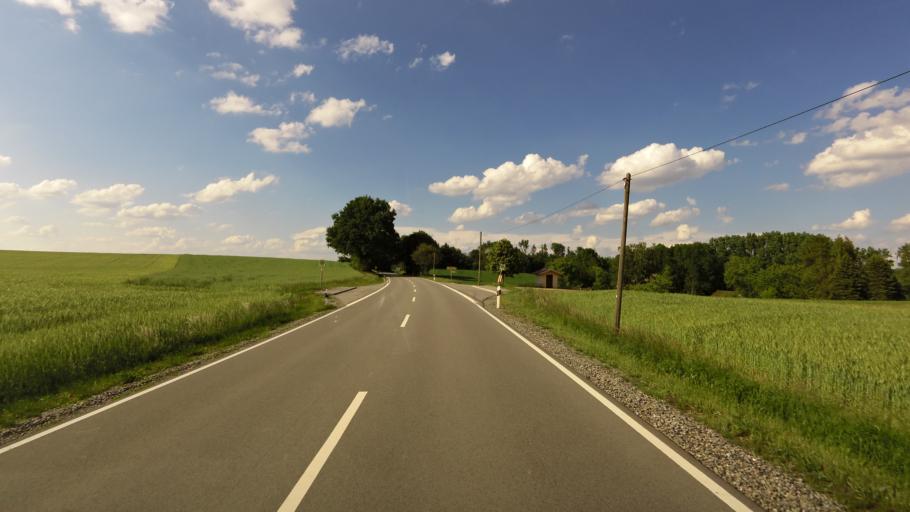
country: DE
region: Bavaria
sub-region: Upper Bavaria
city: Hohenpolding
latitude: 48.4111
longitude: 12.1267
